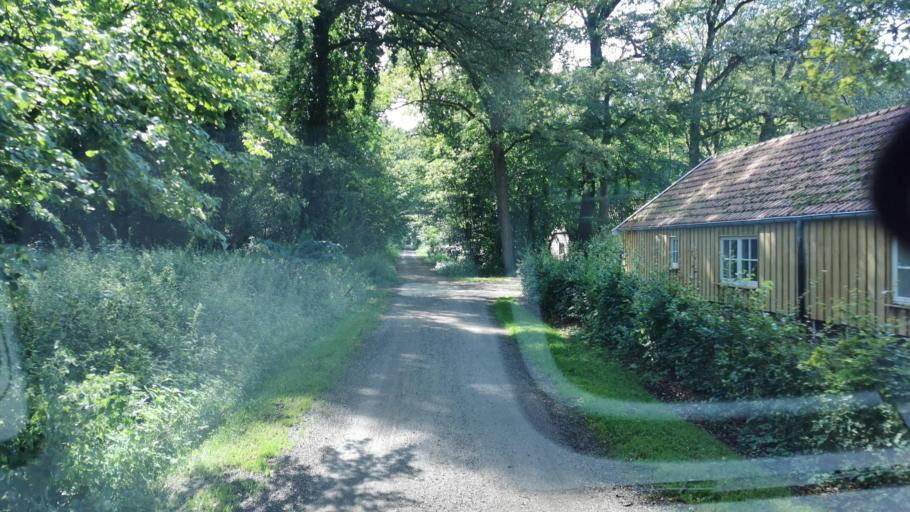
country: NL
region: Overijssel
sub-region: Gemeente Oldenzaal
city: Oldenzaal
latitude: 52.2783
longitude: 6.9591
